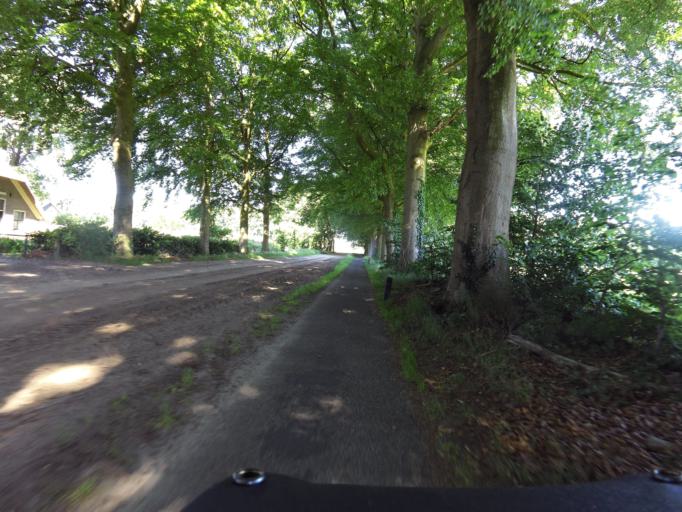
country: NL
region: Overijssel
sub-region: Gemeente Dalfsen
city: Dalfsen
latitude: 52.5116
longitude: 6.3486
